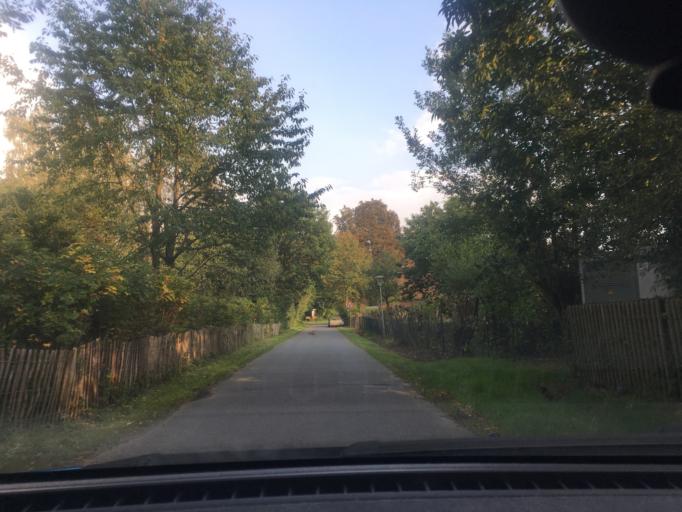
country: DE
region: Lower Saxony
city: Reinstorf
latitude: 53.2025
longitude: 10.5804
